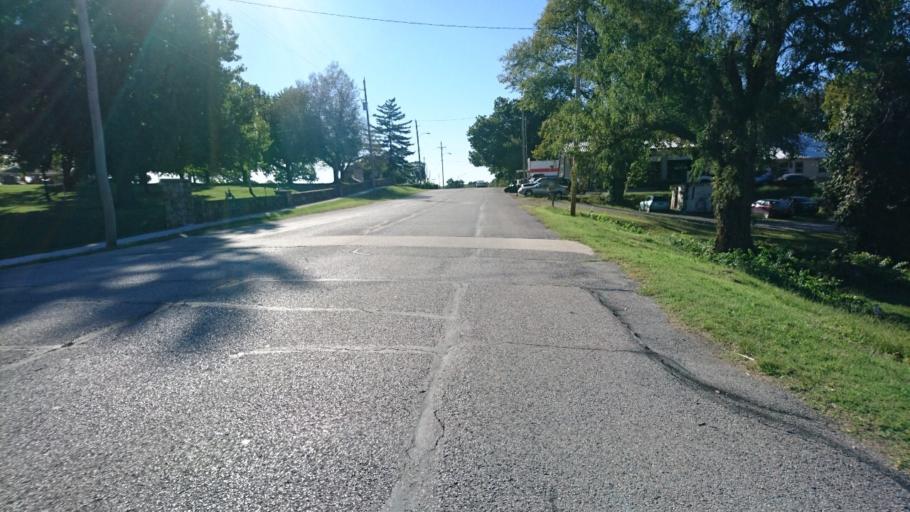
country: US
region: Missouri
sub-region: Jasper County
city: Carthage
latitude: 37.1765
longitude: -94.3362
